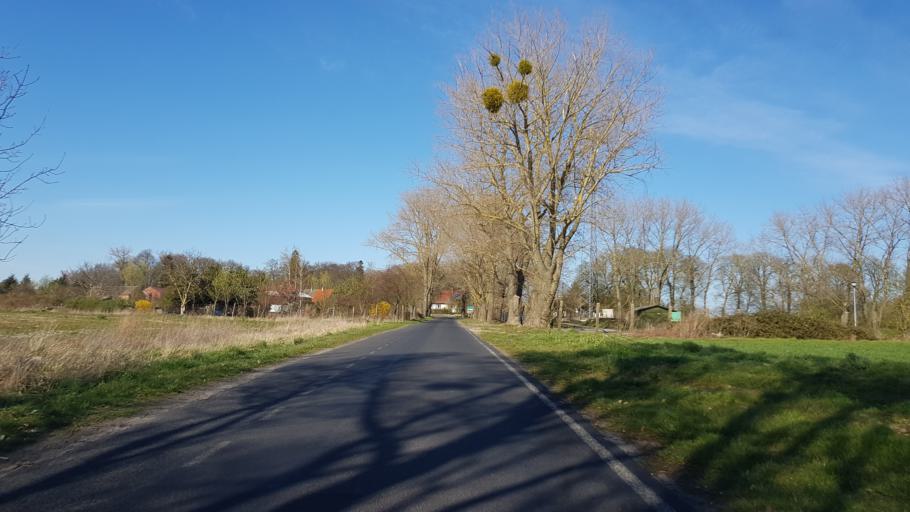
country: PL
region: West Pomeranian Voivodeship
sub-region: Powiat goleniowski
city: Maszewo
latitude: 53.4183
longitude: 15.0532
